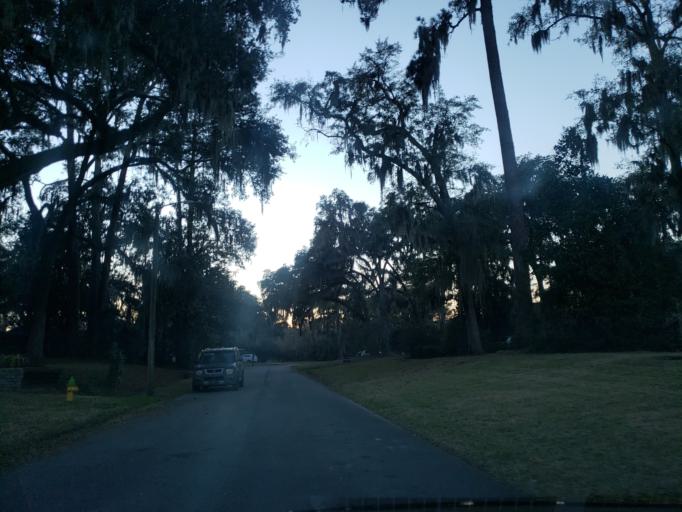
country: US
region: Georgia
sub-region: Chatham County
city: Thunderbolt
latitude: 32.0202
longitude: -81.0855
